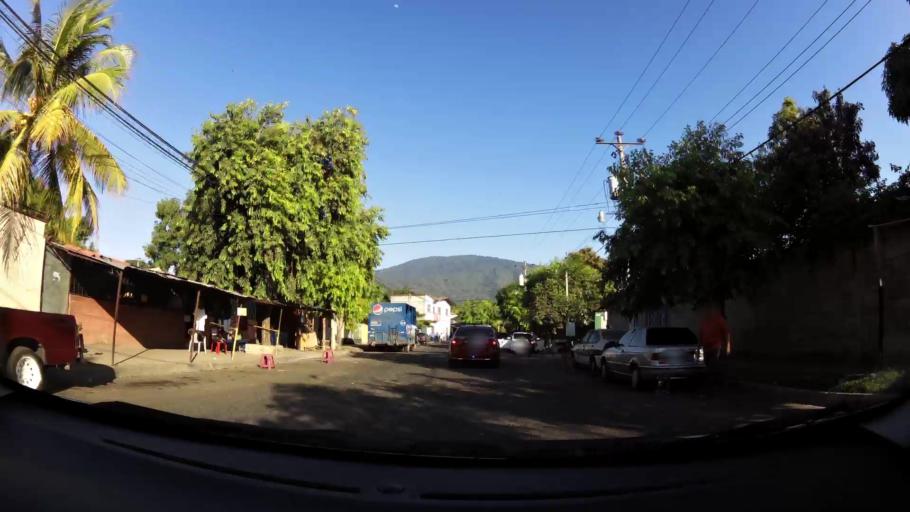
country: SV
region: La Libertad
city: Santa Tecla
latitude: 13.7413
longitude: -89.3574
